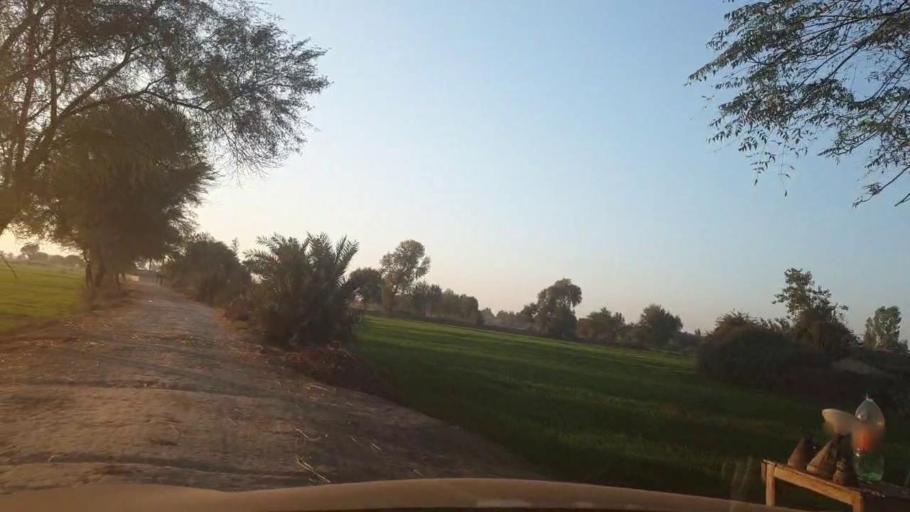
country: PK
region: Sindh
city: Ubauro
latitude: 28.1818
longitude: 69.6042
